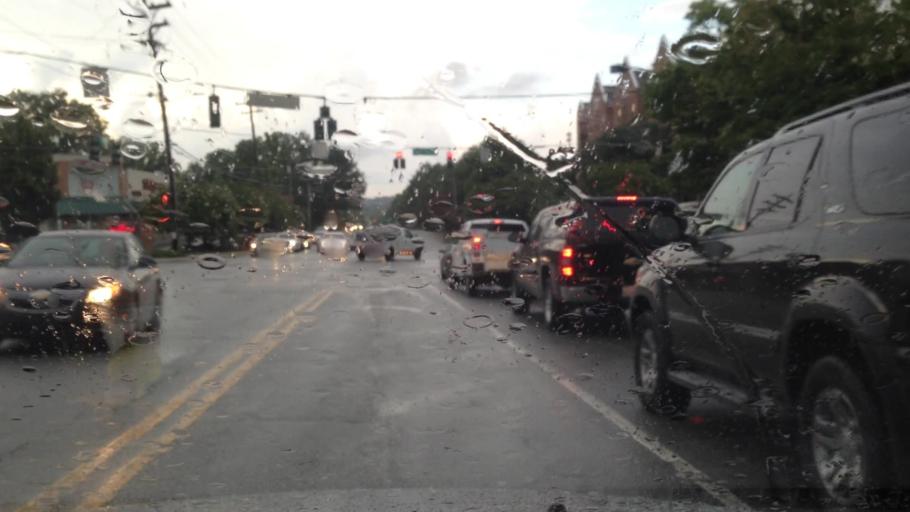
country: US
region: North Carolina
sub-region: Guilford County
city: Greensboro
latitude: 36.0643
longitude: -79.8154
